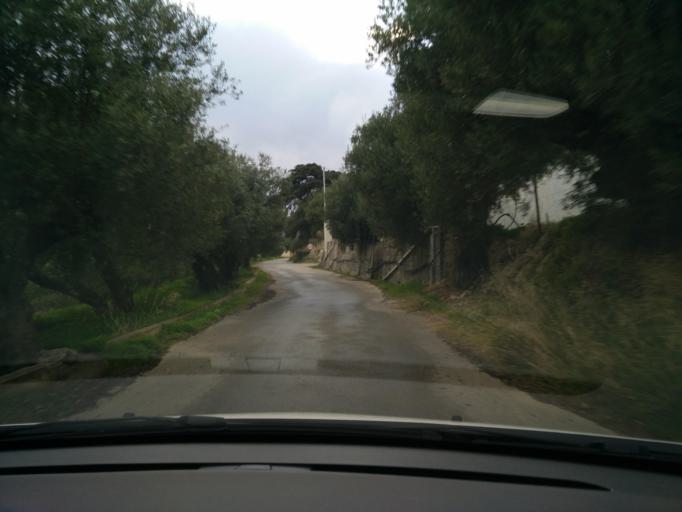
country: GR
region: Crete
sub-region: Nomos Lasithiou
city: Kritsa
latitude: 35.0962
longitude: 25.6895
